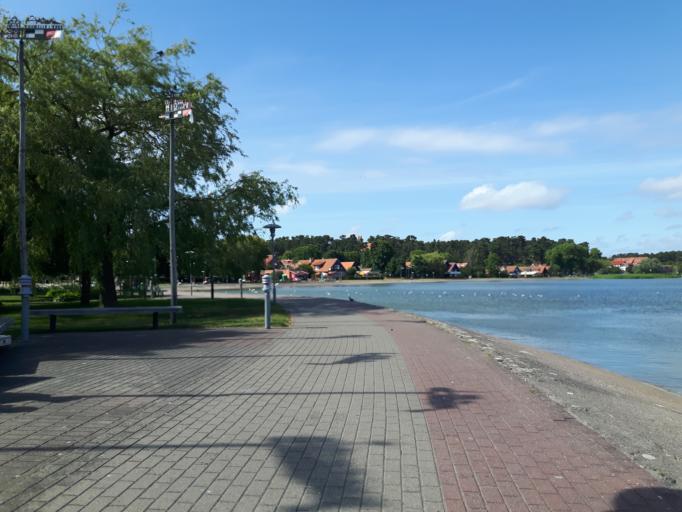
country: LT
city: Nida
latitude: 55.3052
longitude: 21.0087
